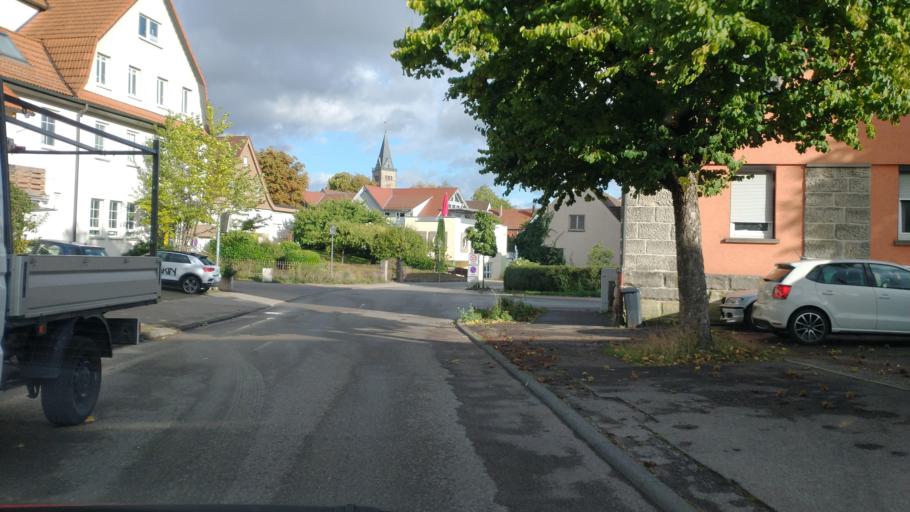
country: DE
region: Baden-Wuerttemberg
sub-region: Regierungsbezirk Stuttgart
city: Welzheim
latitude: 48.8754
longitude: 9.6314
